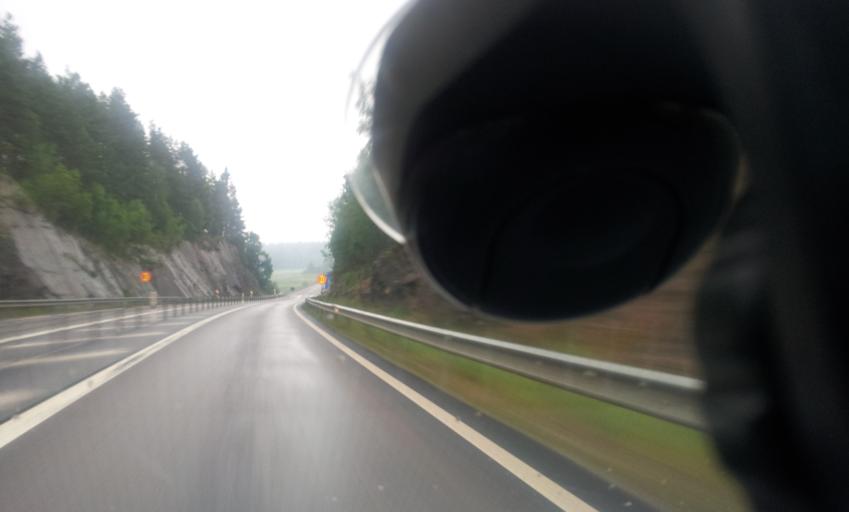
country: SE
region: Kalmar
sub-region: Vasterviks Kommun
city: Gamleby
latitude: 57.9032
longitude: 16.3831
